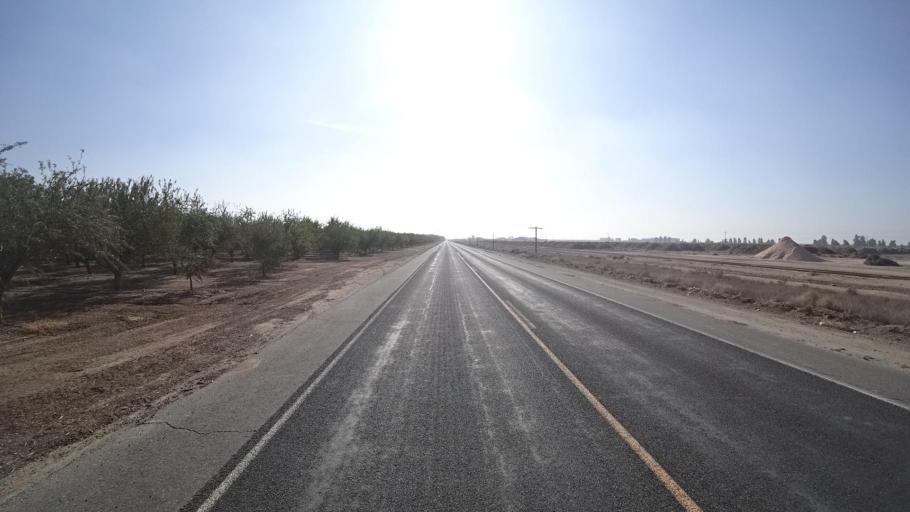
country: US
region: California
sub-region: Kern County
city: McFarland
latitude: 35.6428
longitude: -119.2019
